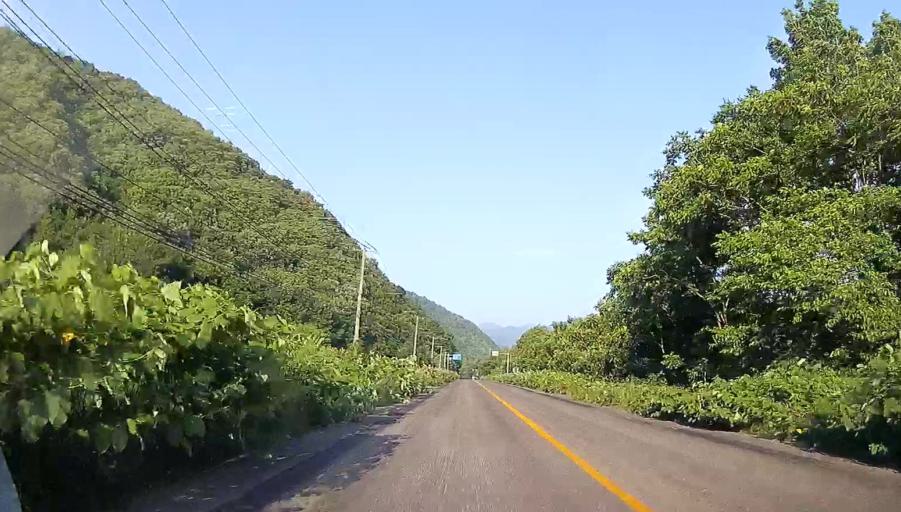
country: JP
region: Hokkaido
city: Shimo-furano
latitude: 42.8952
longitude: 142.4912
